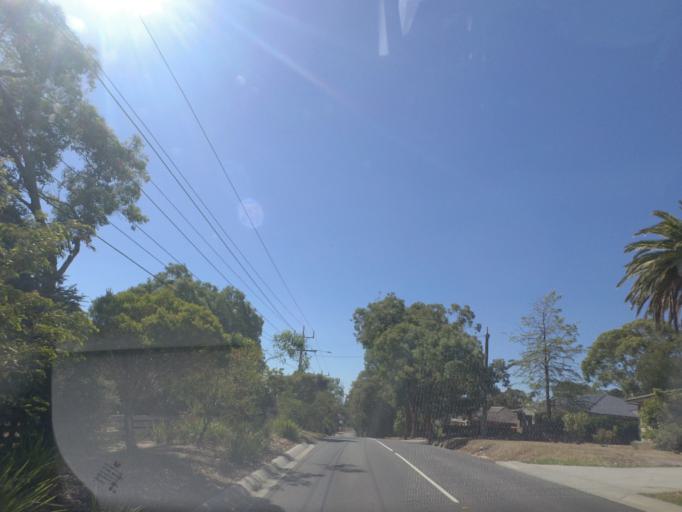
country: AU
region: Victoria
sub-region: Maroondah
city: Warranwood
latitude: -37.7689
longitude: 145.2506
